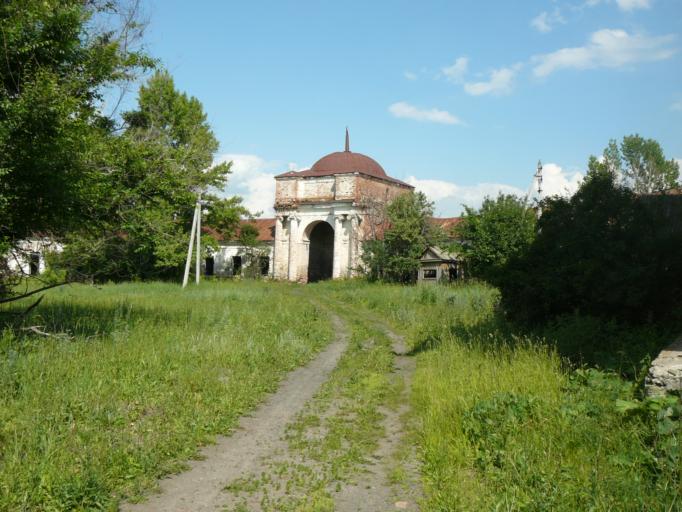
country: RU
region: Penza
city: Serdobsk
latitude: 52.5376
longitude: 44.0579
